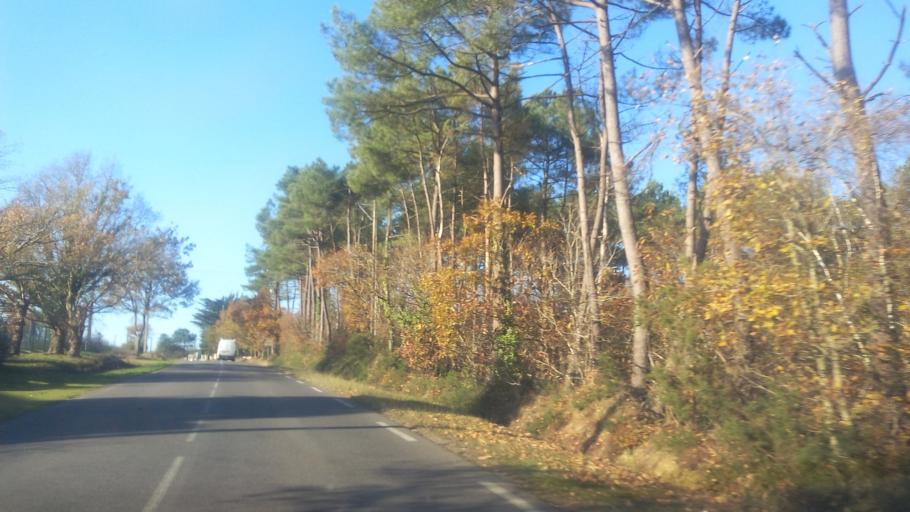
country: FR
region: Brittany
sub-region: Departement du Morbihan
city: Saint-Perreux
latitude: 47.6790
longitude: -2.1186
